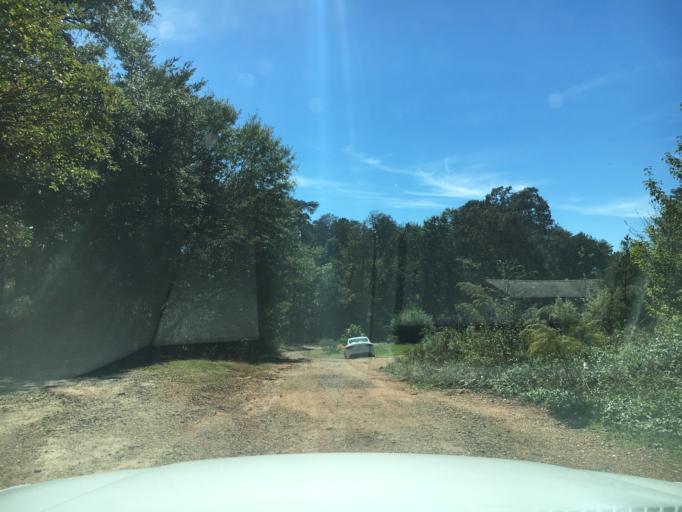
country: US
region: South Carolina
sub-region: Spartanburg County
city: Duncan
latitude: 34.9493
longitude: -82.1678
